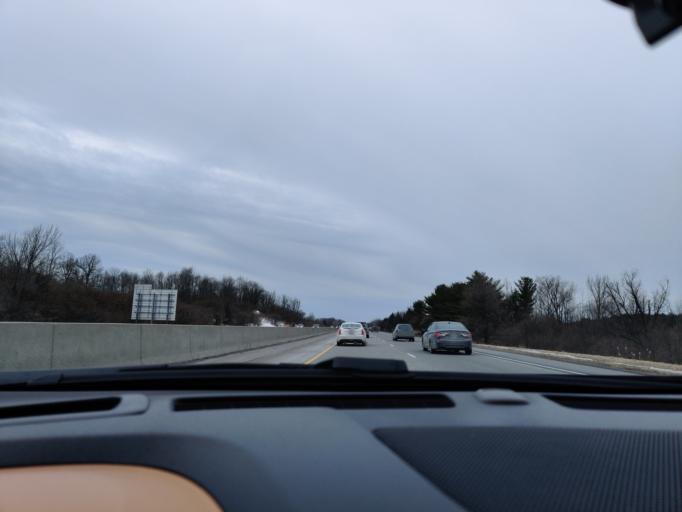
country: CA
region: Ontario
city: Gananoque
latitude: 44.3304
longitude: -76.2484
